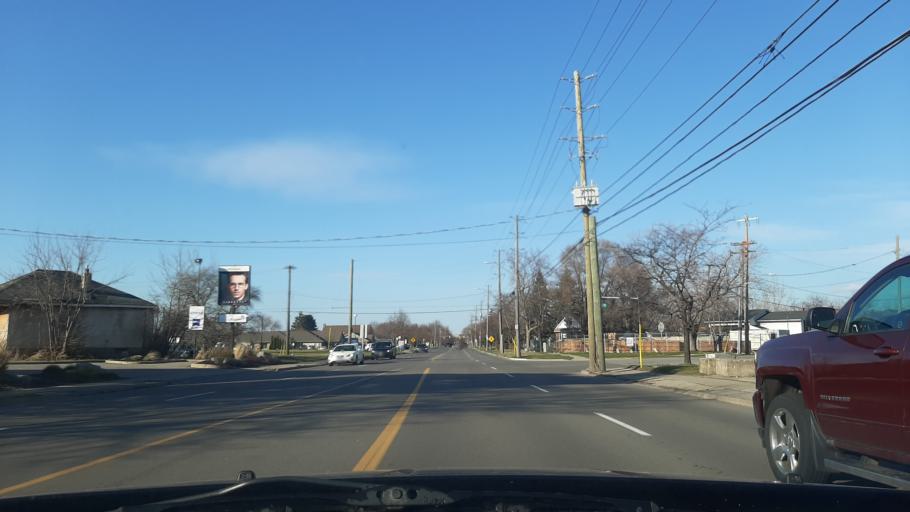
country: CA
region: Ontario
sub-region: Regional Municipality of Niagara
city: St. Catharines
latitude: 43.1821
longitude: -79.2668
